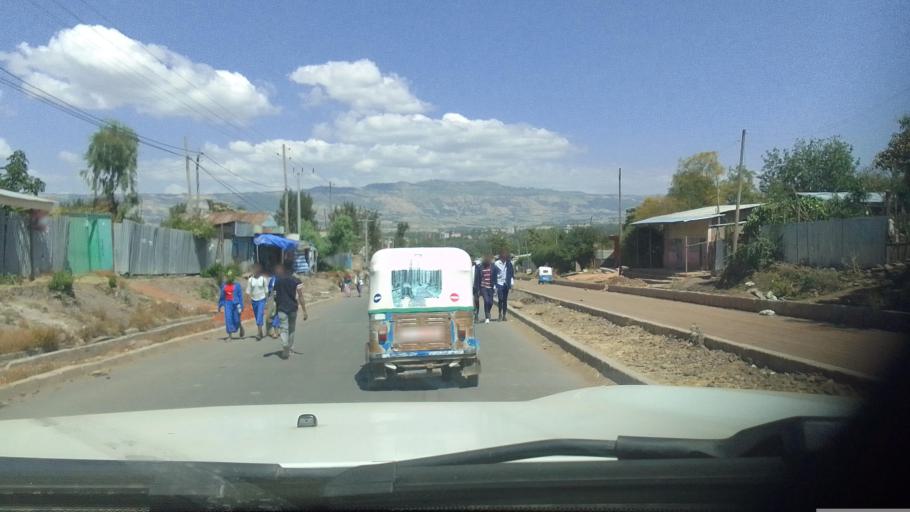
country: ET
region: Oromiya
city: Hagere Hiywet
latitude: 8.9706
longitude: 37.8499
